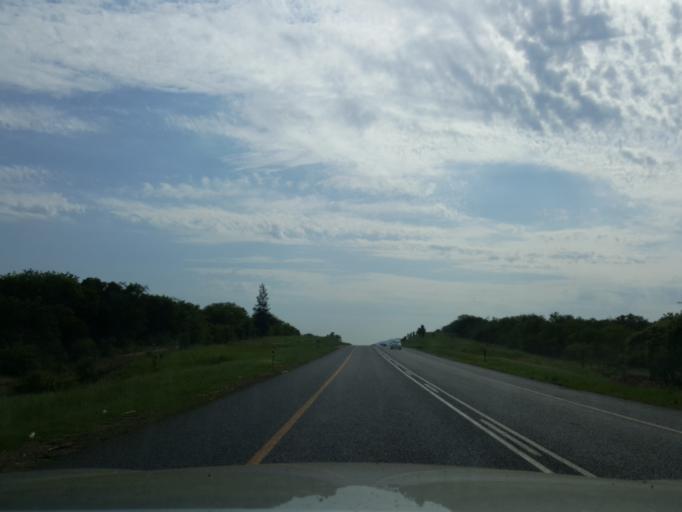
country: SZ
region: Hhohho
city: Ntfonjeni
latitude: -25.5167
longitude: 31.4427
